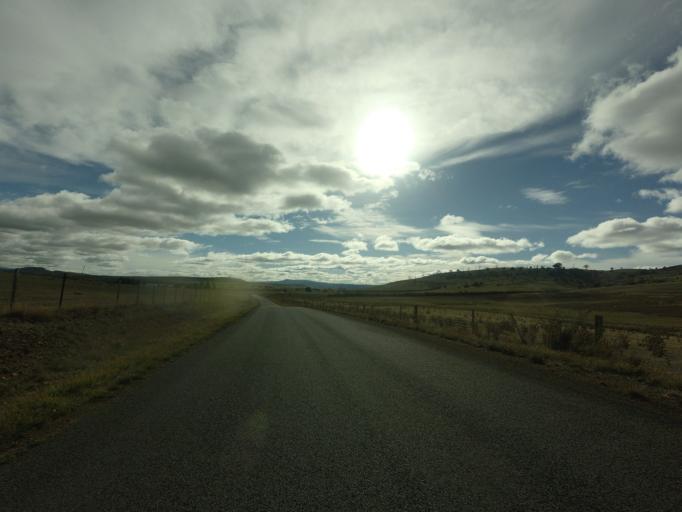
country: AU
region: Tasmania
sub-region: Brighton
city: Bridgewater
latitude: -42.3696
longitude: 147.3509
